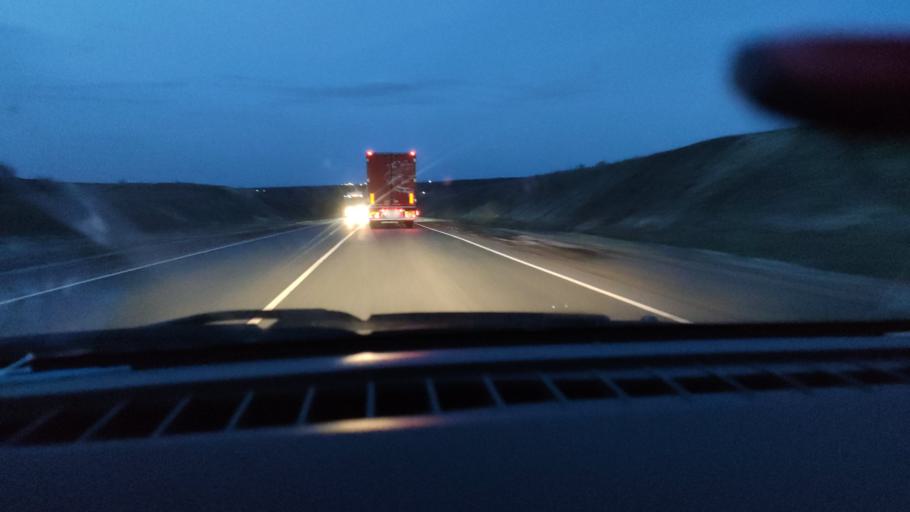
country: RU
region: Saratov
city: Sennoy
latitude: 52.1400
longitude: 46.8859
